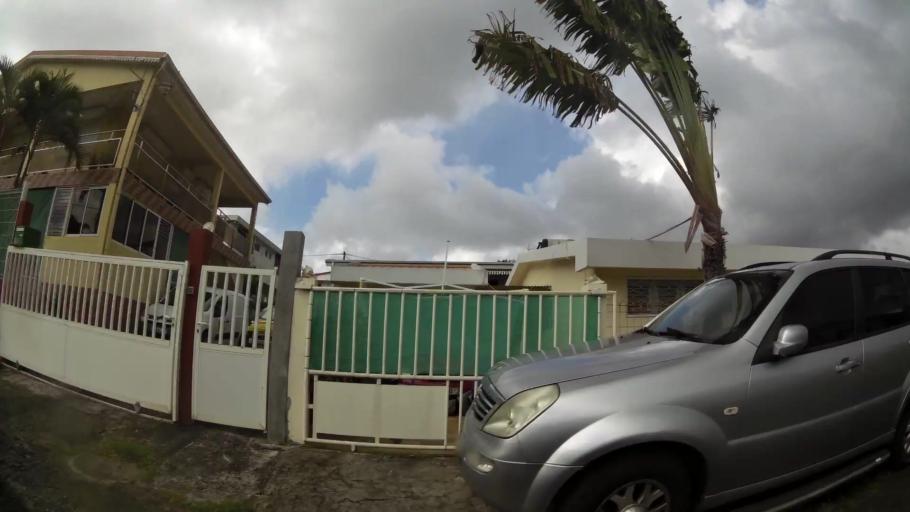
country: MQ
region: Martinique
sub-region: Martinique
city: Sainte-Luce
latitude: 14.4655
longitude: -60.9301
